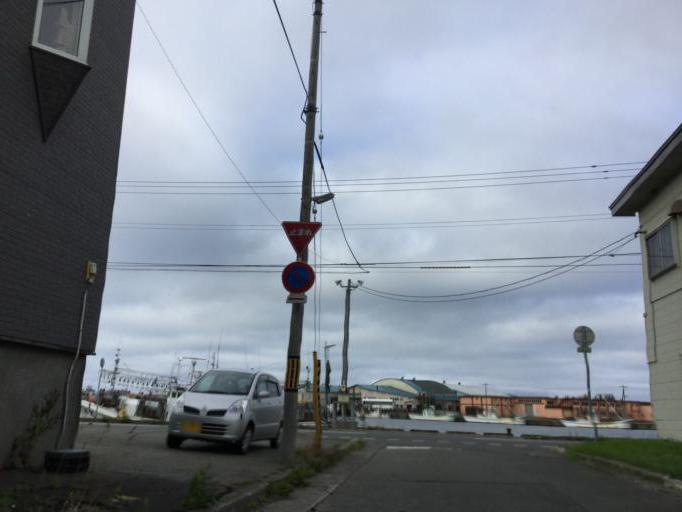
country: JP
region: Hokkaido
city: Wakkanai
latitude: 45.4041
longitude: 141.6778
